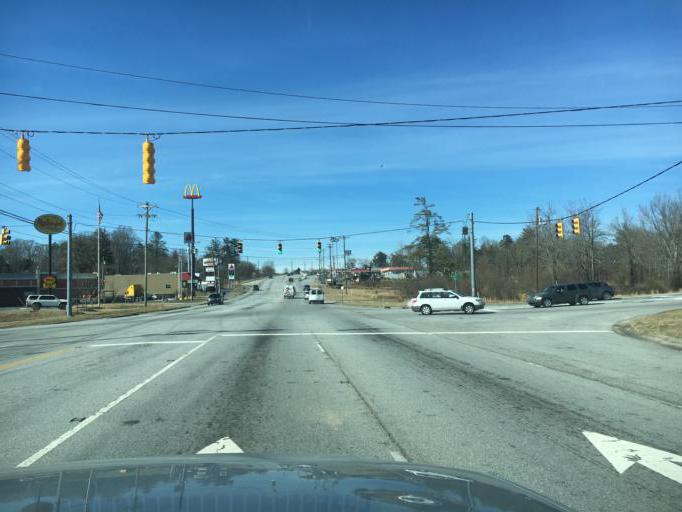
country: US
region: North Carolina
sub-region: Henderson County
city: Mountain Home
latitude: 35.3950
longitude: -82.5050
